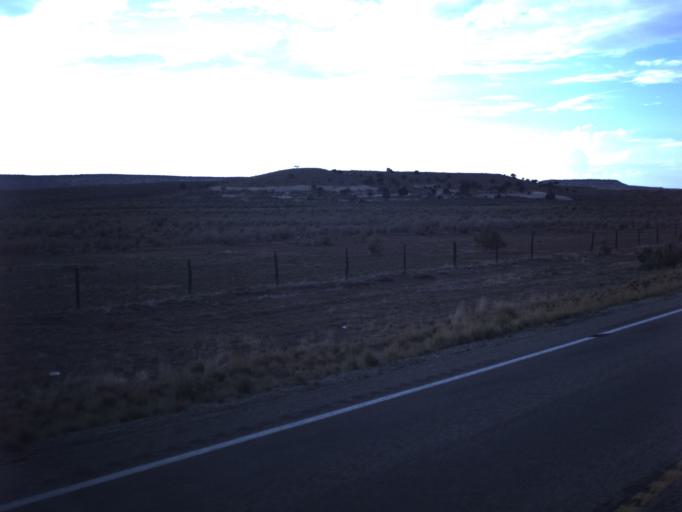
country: US
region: Utah
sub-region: San Juan County
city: Monticello
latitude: 38.0512
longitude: -109.3423
